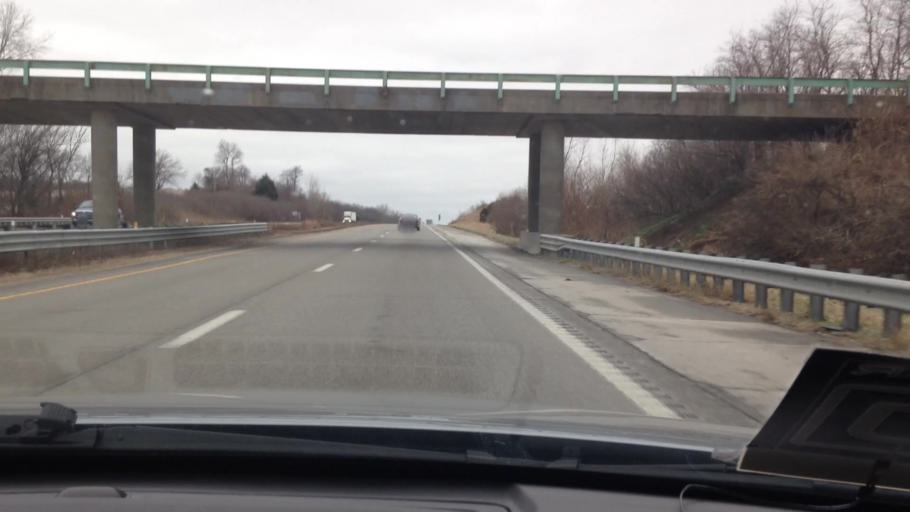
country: US
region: Missouri
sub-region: Platte County
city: Platte City
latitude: 39.4989
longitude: -94.7864
